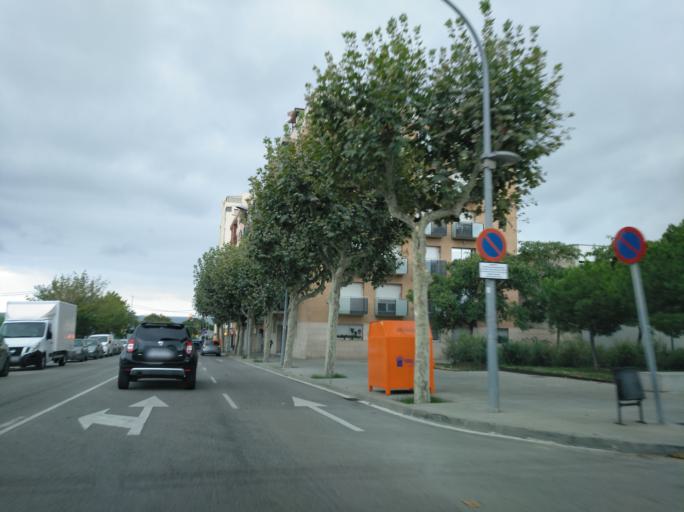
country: ES
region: Catalonia
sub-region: Provincia de Barcelona
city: Mataro
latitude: 41.5424
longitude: 2.4555
